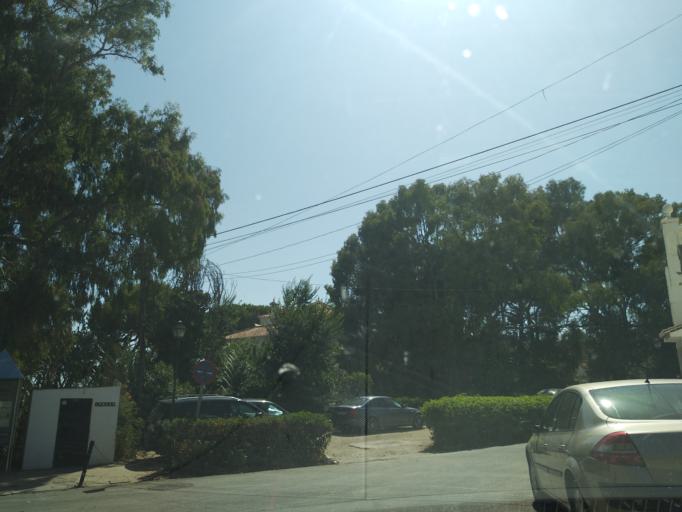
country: ES
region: Andalusia
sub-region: Provincia de Malaga
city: Valdes
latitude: 36.7157
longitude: -4.2011
